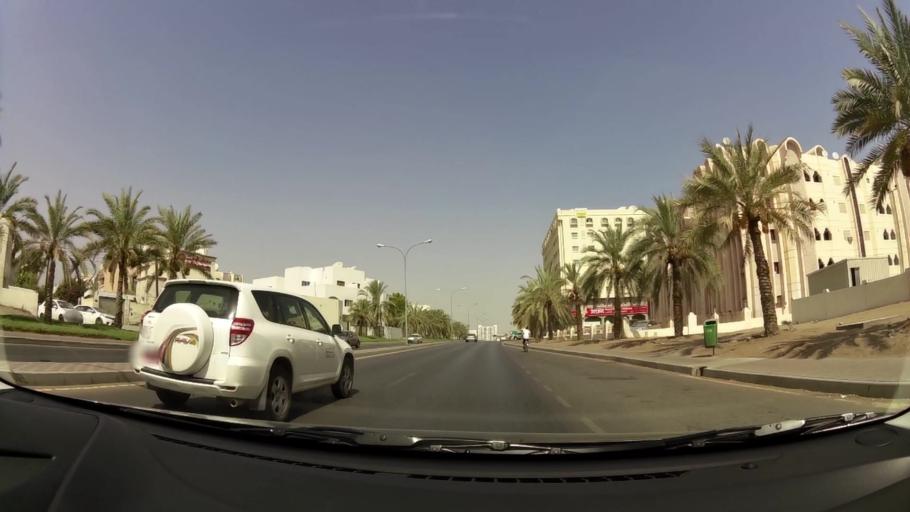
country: OM
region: Muhafazat Masqat
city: Bawshar
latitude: 23.5933
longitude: 58.4223
